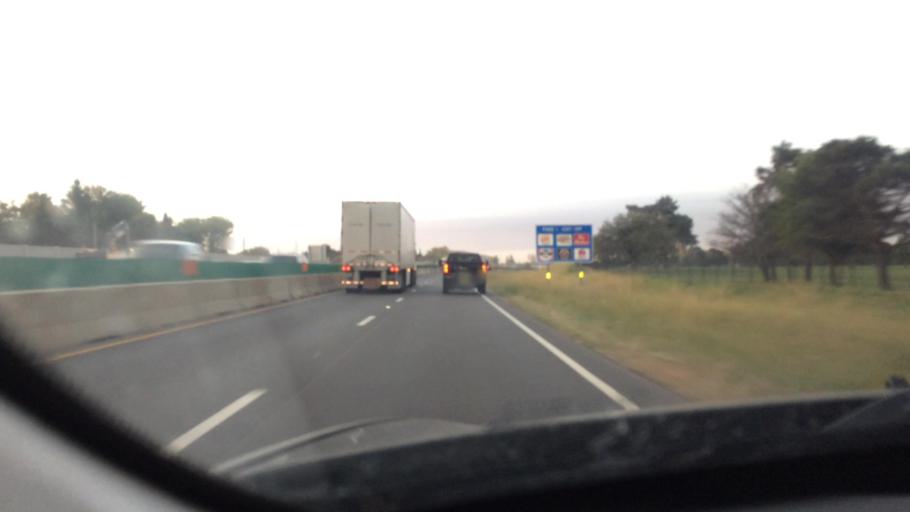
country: US
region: Ohio
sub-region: Hancock County
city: Findlay
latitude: 41.0785
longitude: -83.6602
